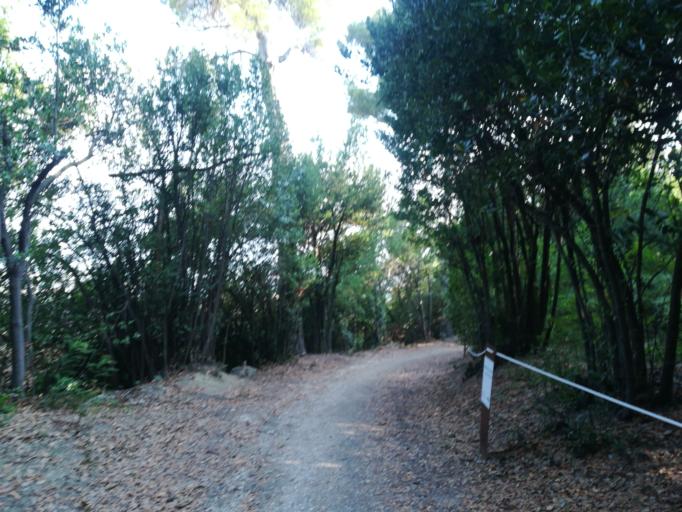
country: IT
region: The Marches
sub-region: Provincia di Macerata
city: Villa Potenza
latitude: 43.2945
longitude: 13.4214
